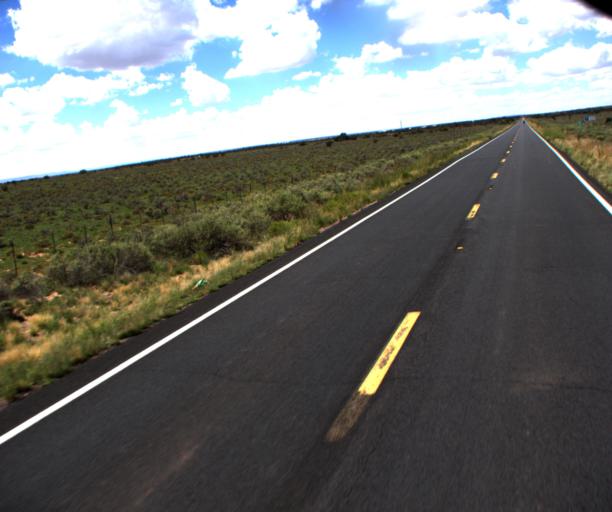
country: US
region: Arizona
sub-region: Coconino County
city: Williams
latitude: 35.6320
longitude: -112.1189
